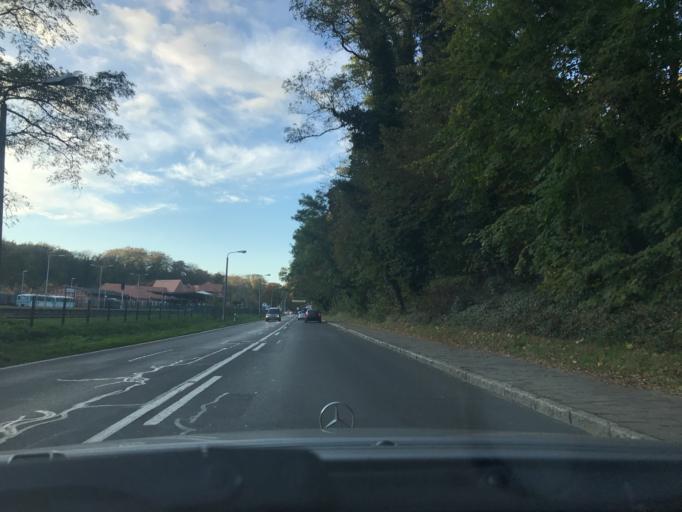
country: DE
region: Mecklenburg-Vorpommern
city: Seebad Heringsdorf
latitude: 53.9481
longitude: 14.1735
